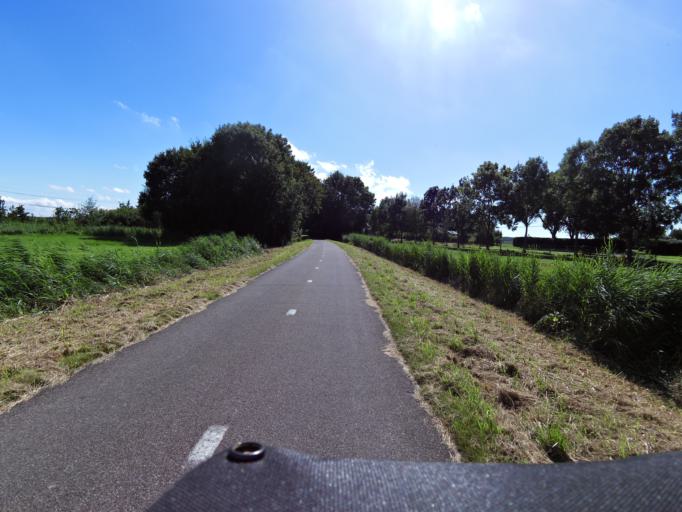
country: NL
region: South Holland
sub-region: Gemeente Spijkenisse
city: Spijkenisse
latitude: 51.8366
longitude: 4.2861
